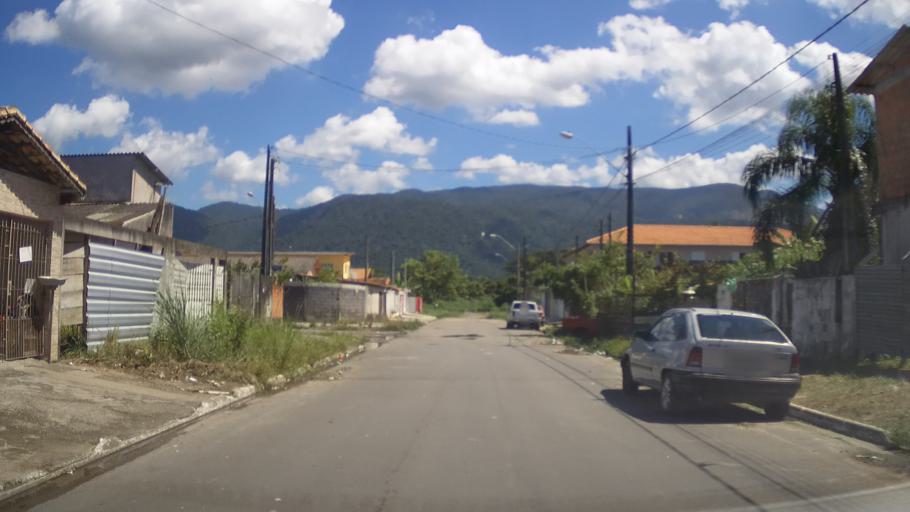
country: BR
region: Sao Paulo
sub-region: Mongagua
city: Mongagua
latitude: -24.0561
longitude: -46.5550
